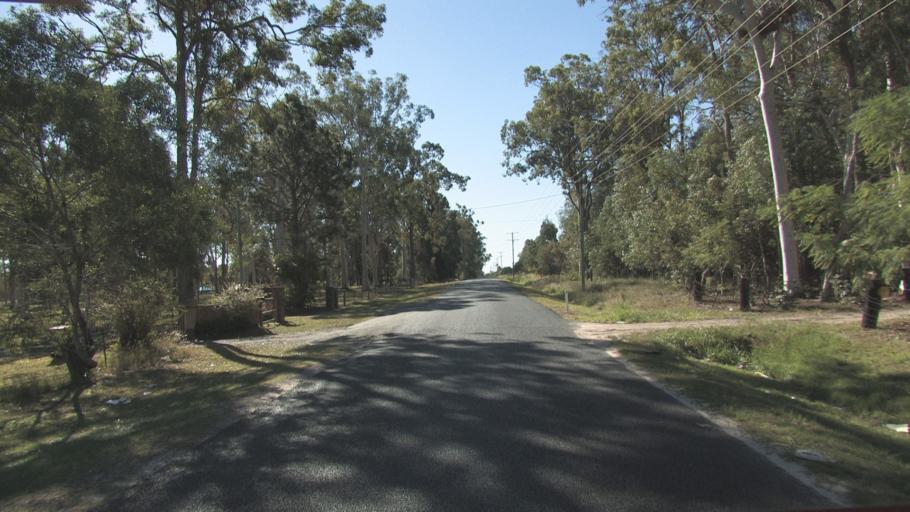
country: AU
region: Queensland
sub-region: Logan
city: Logan Reserve
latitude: -27.7280
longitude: 153.0727
